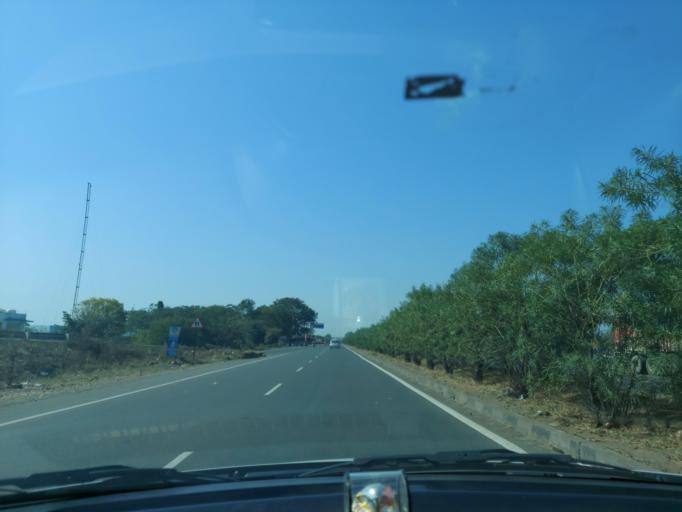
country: IN
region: Madhya Pradesh
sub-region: Indore
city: Manpur
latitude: 22.4270
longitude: 75.6118
